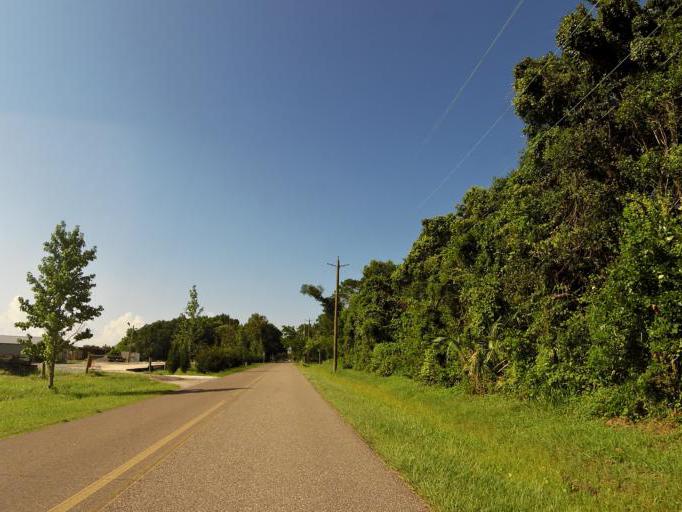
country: US
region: Florida
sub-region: Nassau County
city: Fernandina Beach
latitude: 30.6640
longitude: -81.4641
